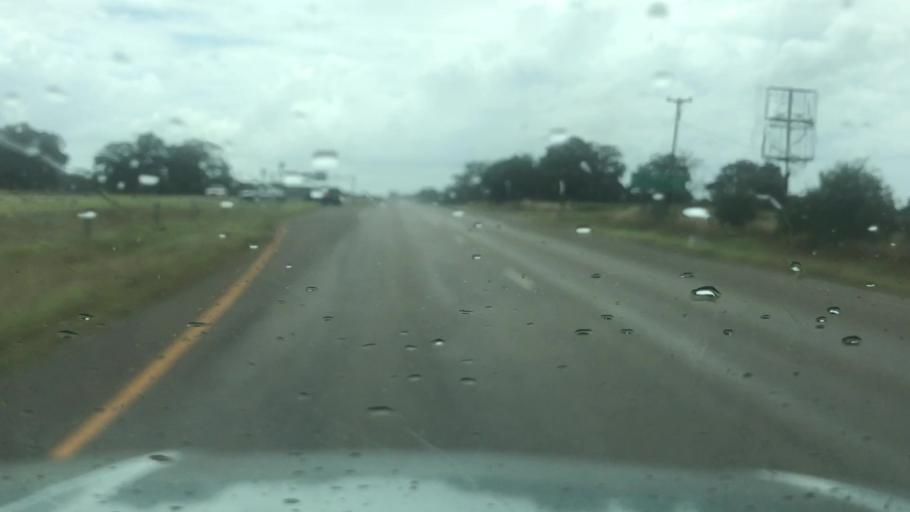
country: US
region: Texas
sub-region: Colorado County
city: Columbus
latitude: 29.7389
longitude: -96.5885
